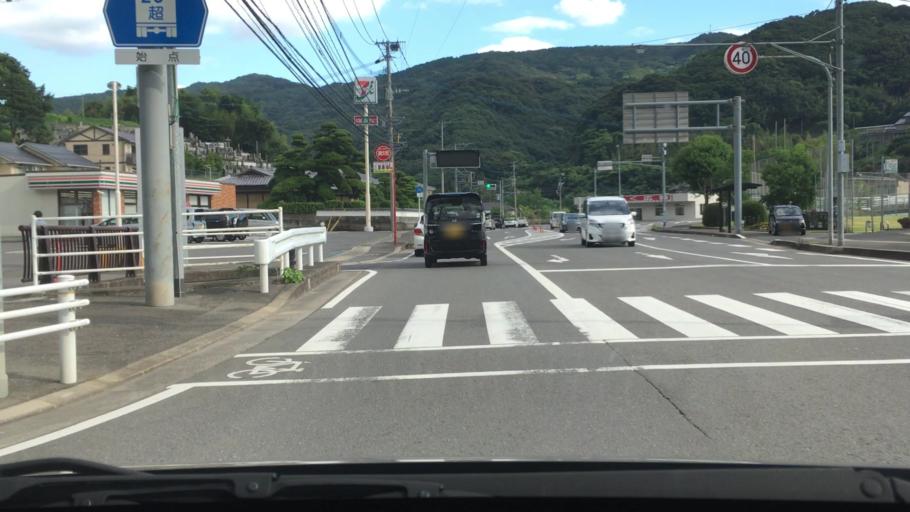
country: JP
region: Nagasaki
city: Togitsu
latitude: 32.8275
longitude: 129.7840
